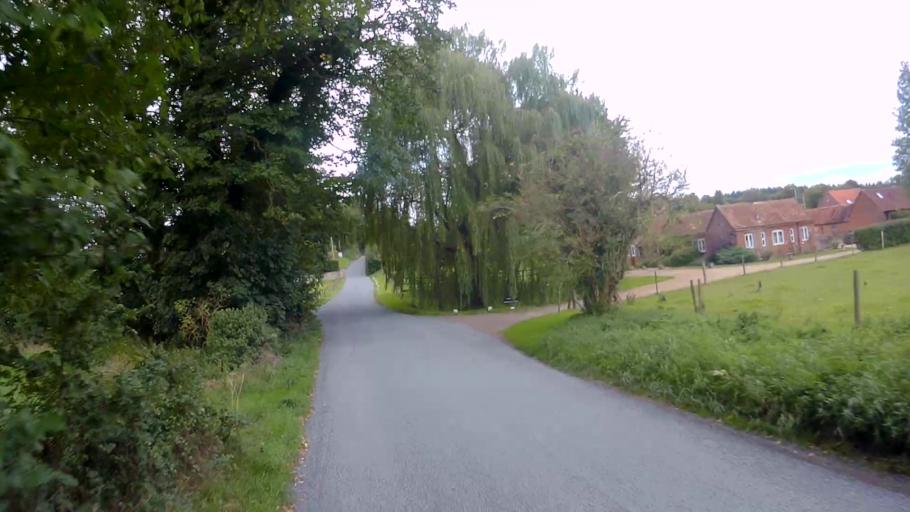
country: GB
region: England
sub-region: Hampshire
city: Overton
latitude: 51.2145
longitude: -1.2008
